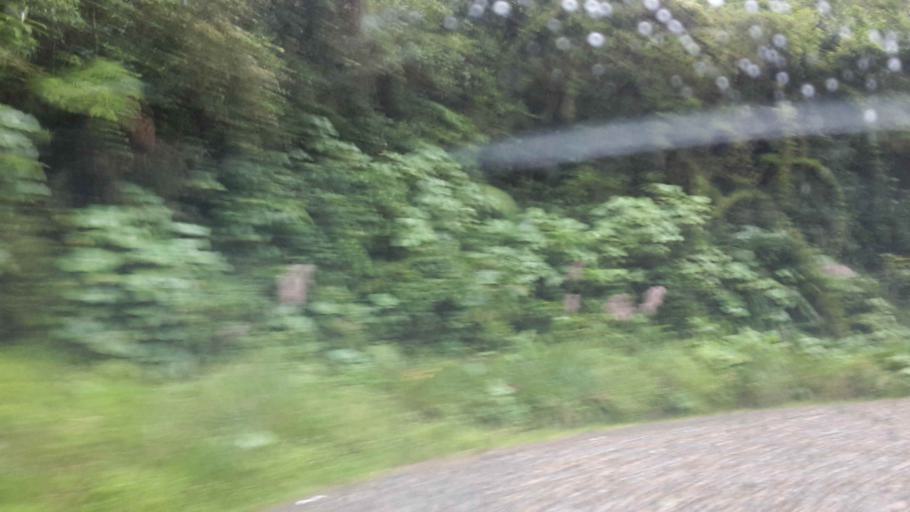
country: BO
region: Cochabamba
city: Colomi
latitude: -17.1556
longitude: -65.9057
